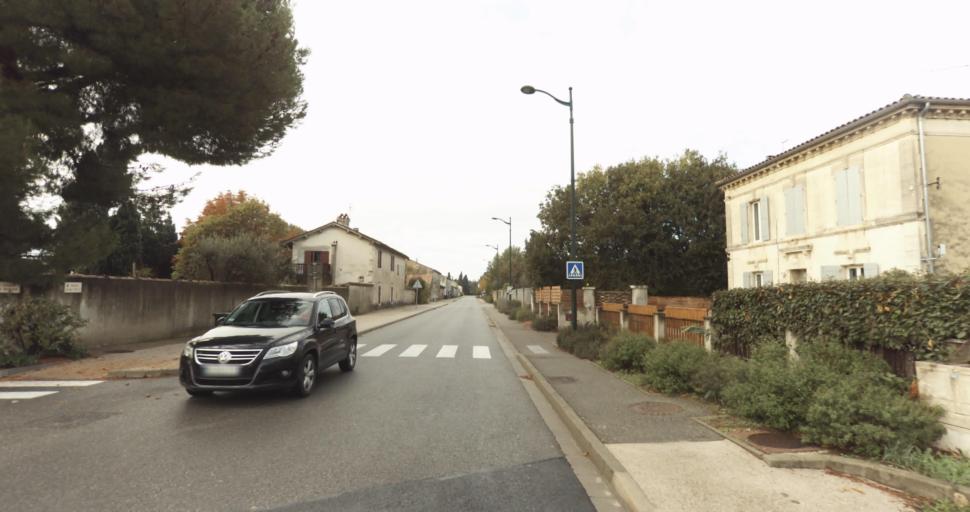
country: FR
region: Provence-Alpes-Cote d'Azur
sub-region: Departement des Bouches-du-Rhone
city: Rognonas
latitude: 43.8975
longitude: 4.7968
